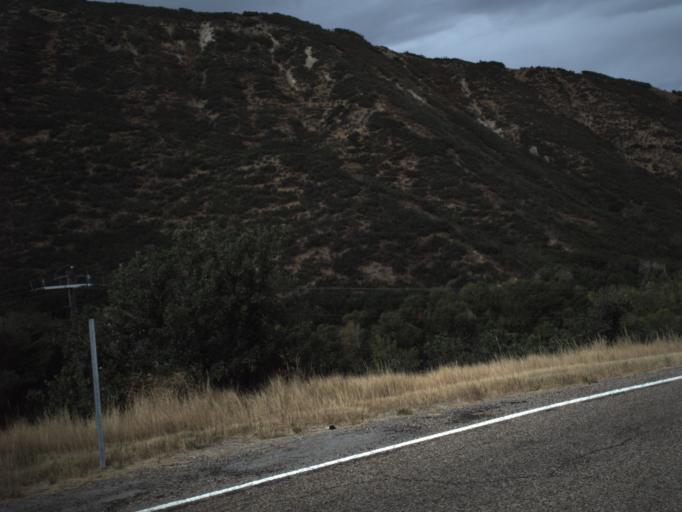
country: US
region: Utah
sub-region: Morgan County
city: Morgan
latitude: 40.9242
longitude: -111.6095
